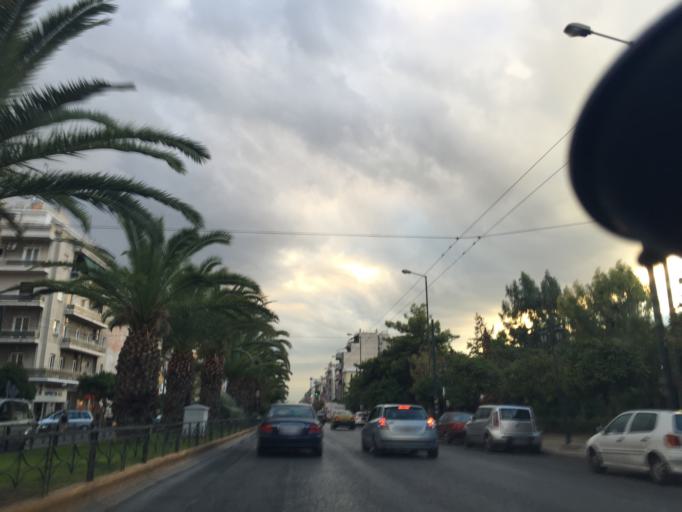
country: GR
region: Attica
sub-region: Nomarchia Athinas
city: Kallithea
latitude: 37.9610
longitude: 23.7093
